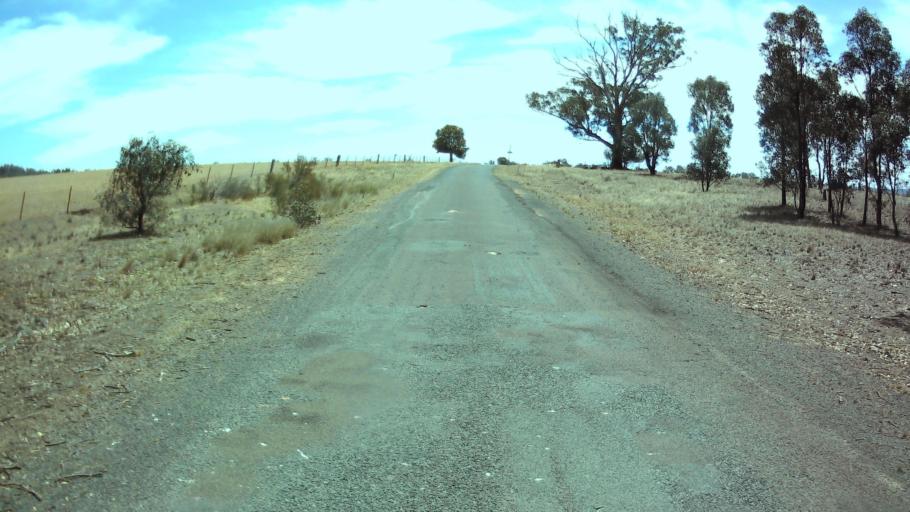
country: AU
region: New South Wales
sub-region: Weddin
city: Grenfell
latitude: -33.7489
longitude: 148.2073
